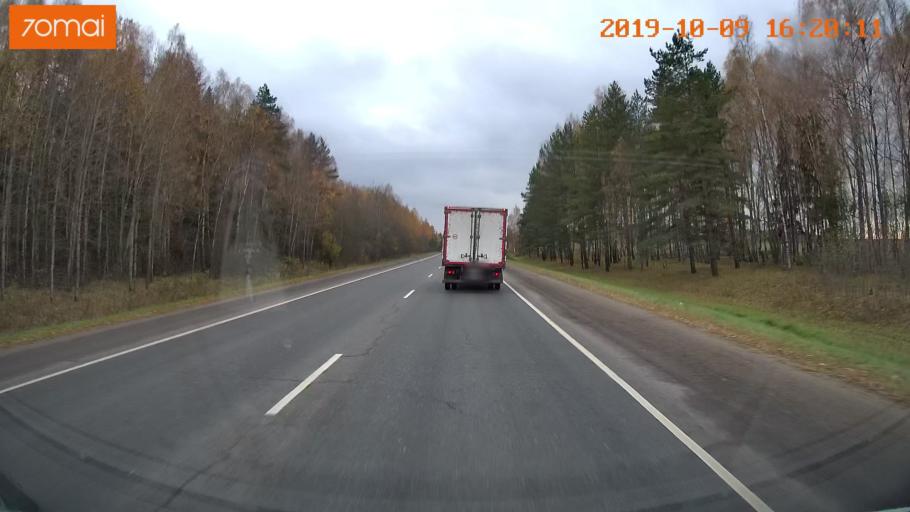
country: RU
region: Kostroma
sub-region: Kostromskoy Rayon
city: Kostroma
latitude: 57.7096
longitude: 40.8928
